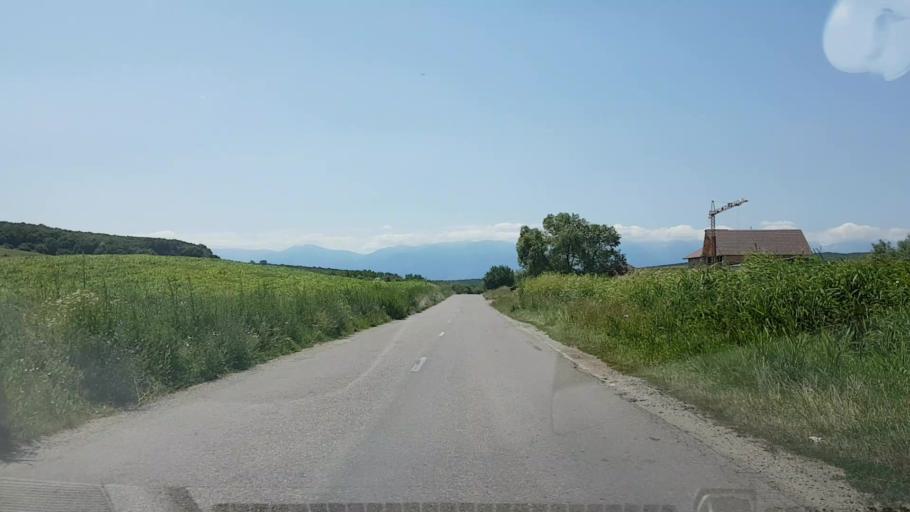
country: RO
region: Brasov
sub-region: Comuna Cincu
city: Cincu
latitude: 45.9049
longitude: 24.8117
